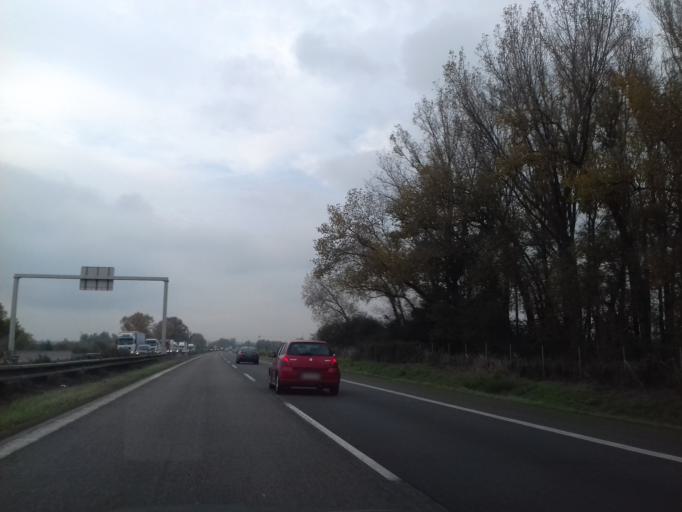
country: SK
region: Bratislavsky
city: Stupava
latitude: 48.2230
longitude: 17.0275
